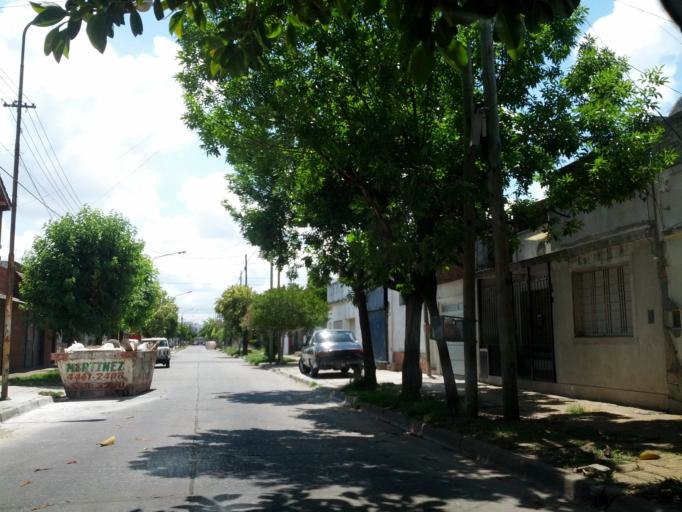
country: AR
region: Buenos Aires
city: San Justo
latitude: -34.6463
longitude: -58.5477
